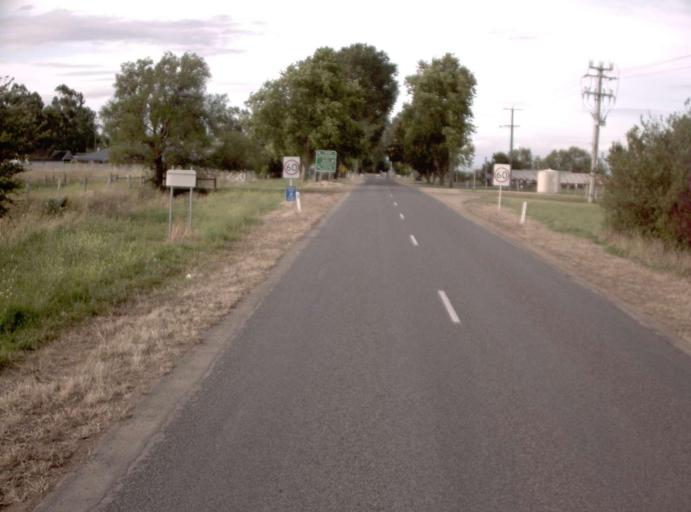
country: AU
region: Victoria
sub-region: Wellington
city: Heyfield
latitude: -37.9652
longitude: 146.8913
